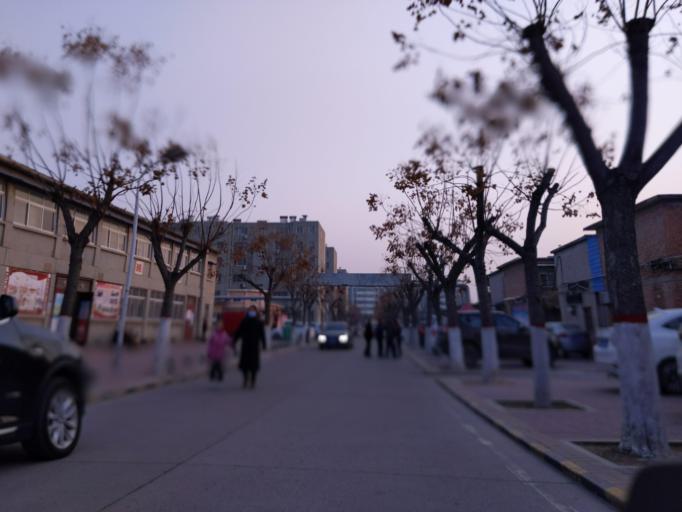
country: CN
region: Henan Sheng
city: Zhongyuanlu
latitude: 35.7724
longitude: 115.0887
